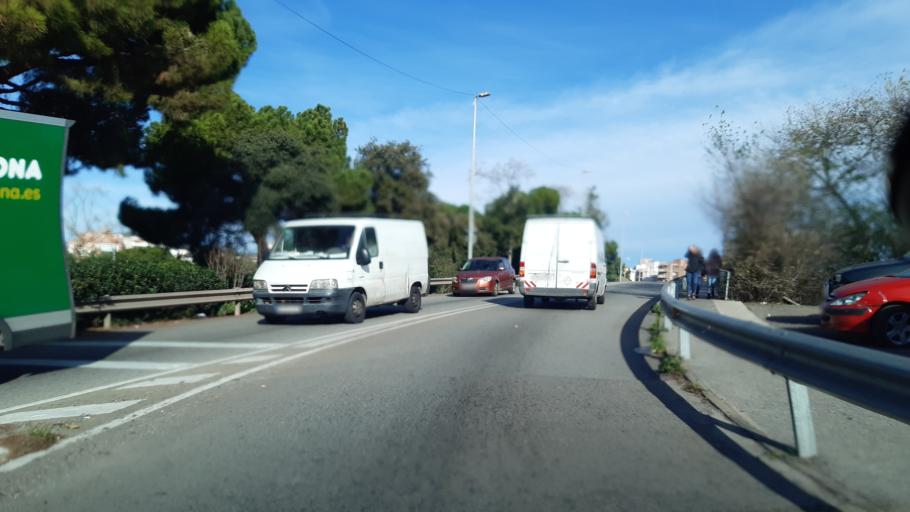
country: ES
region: Catalonia
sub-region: Provincia de Barcelona
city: L'Hospitalet de Llobregat
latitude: 41.3635
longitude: 2.1159
